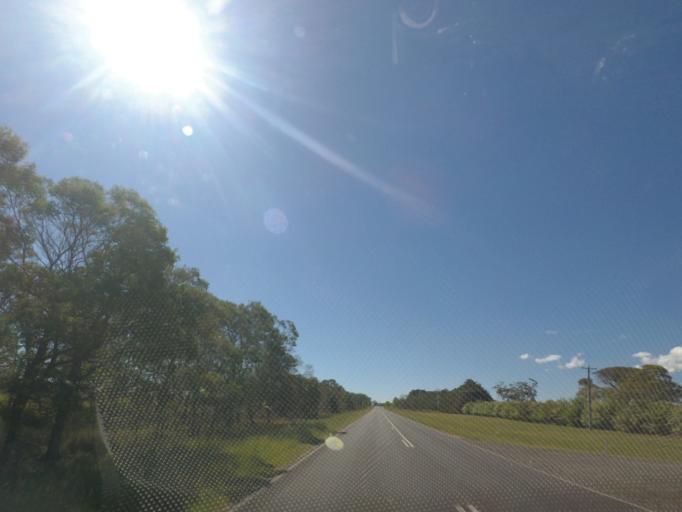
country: AU
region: Victoria
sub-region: Moorabool
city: Bacchus Marsh
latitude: -37.6344
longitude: 144.2168
